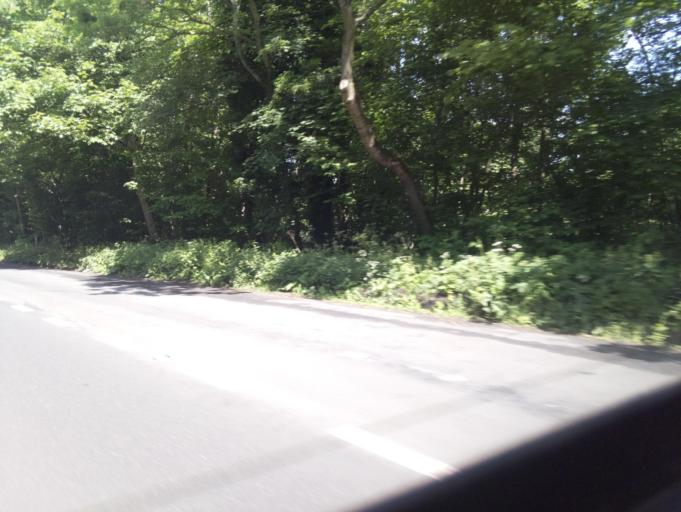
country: GB
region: England
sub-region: North Lincolnshire
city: Broughton
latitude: 53.5505
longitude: -0.5653
